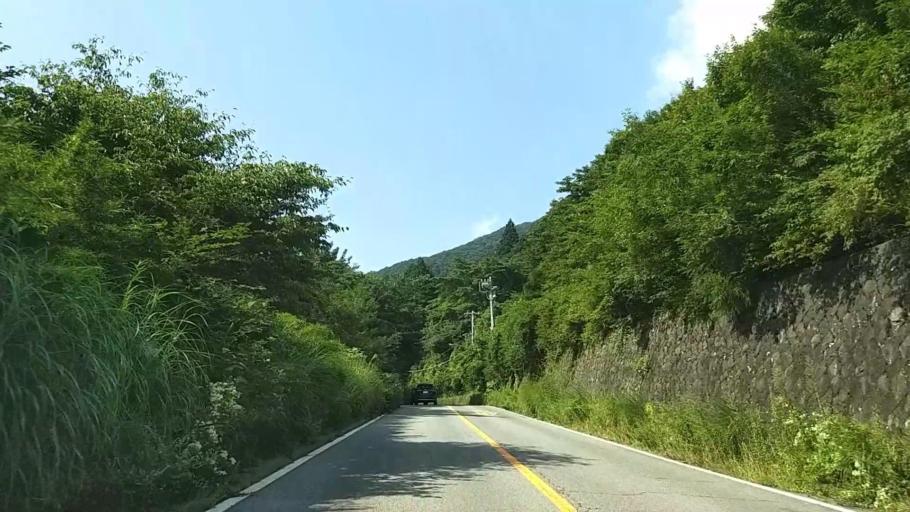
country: JP
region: Kanagawa
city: Hakone
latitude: 35.2160
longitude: 139.0131
